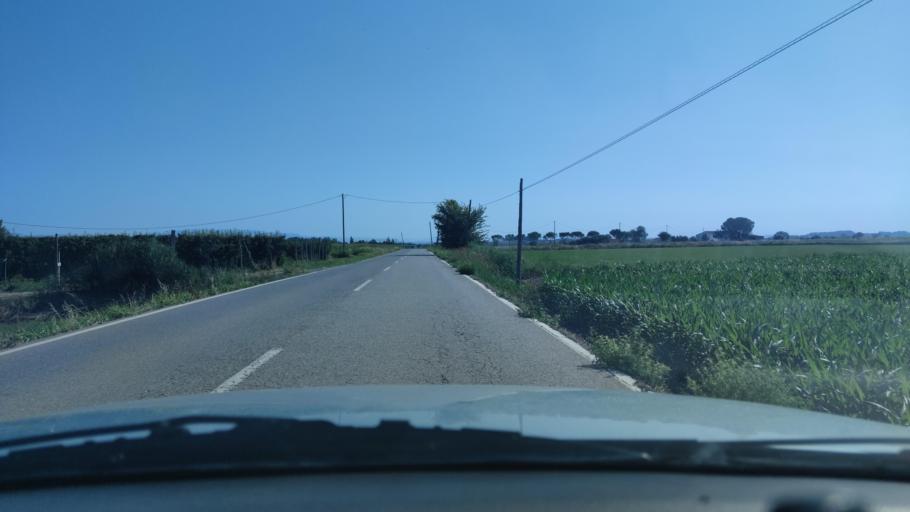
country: ES
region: Catalonia
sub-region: Provincia de Lleida
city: Bellvis
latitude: 41.6514
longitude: 0.8021
